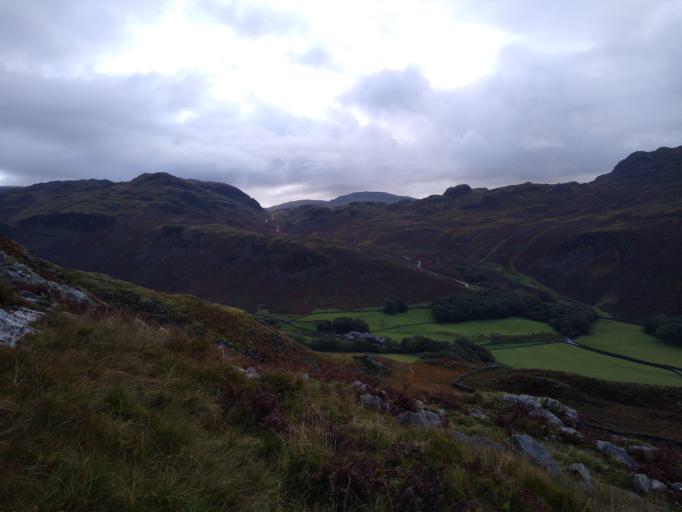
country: GB
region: England
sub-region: Cumbria
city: Millom
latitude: 54.4033
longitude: -3.2252
